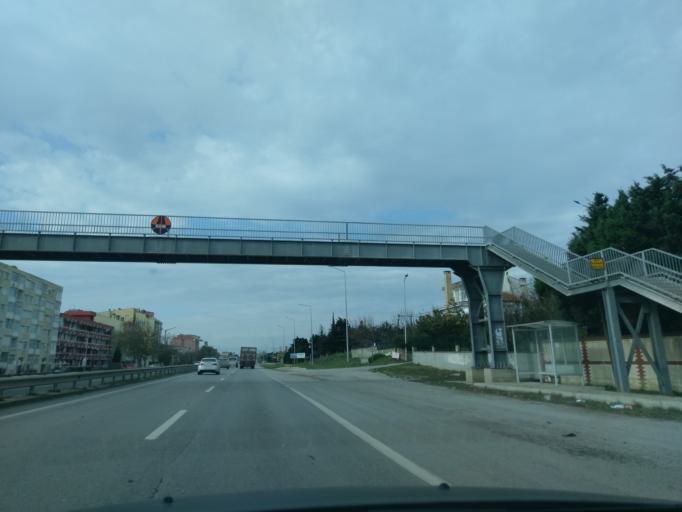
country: TR
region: Istanbul
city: Celaliye
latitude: 41.0458
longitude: 28.4073
